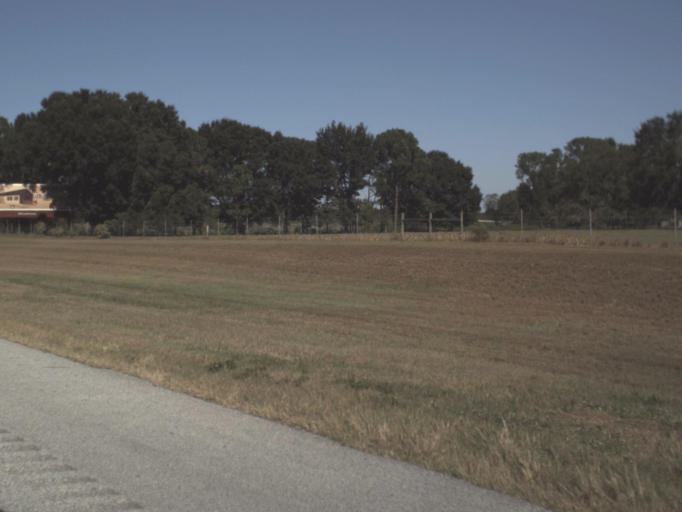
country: US
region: Florida
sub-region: Lake County
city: Hawthorne
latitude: 28.6913
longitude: -81.8710
